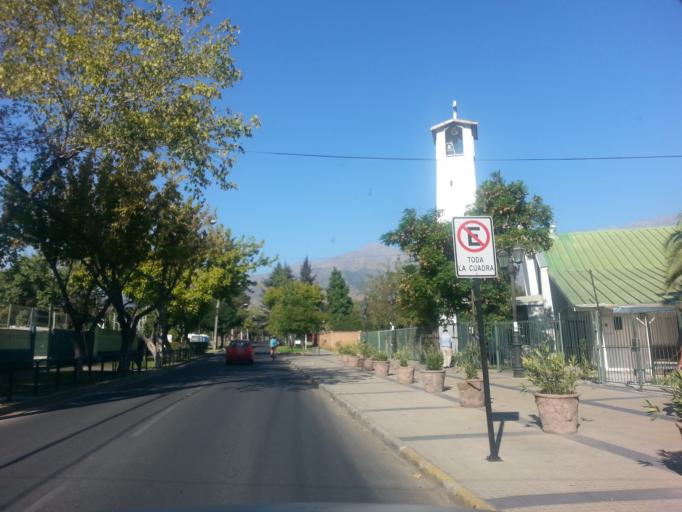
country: CL
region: Santiago Metropolitan
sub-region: Provincia de Santiago
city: Villa Presidente Frei, Nunoa, Santiago, Chile
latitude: -33.4251
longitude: -70.5623
